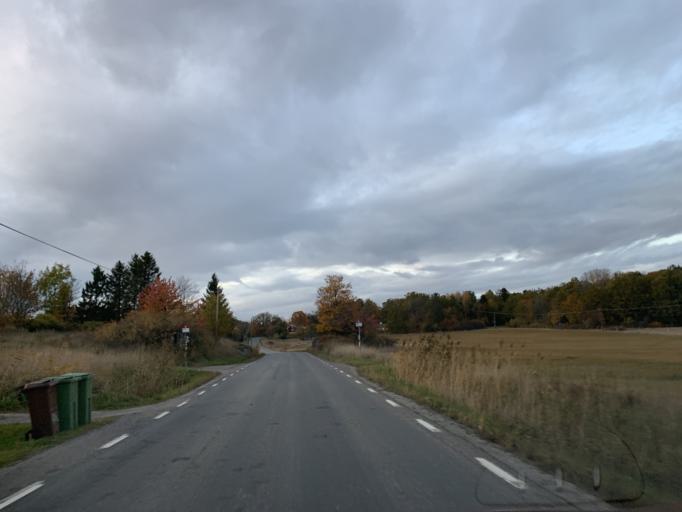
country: SE
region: Stockholm
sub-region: Nynashamns Kommun
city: Osmo
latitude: 58.9249
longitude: 17.7736
